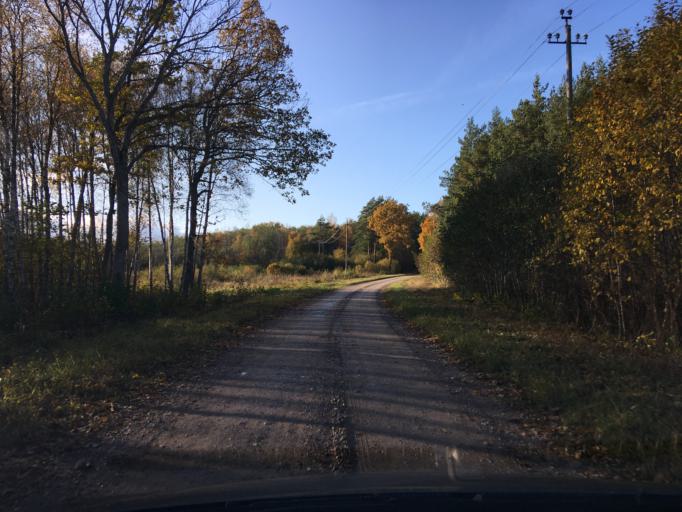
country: EE
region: Laeaene
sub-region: Lihula vald
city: Lihula
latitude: 58.5683
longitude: 23.7550
